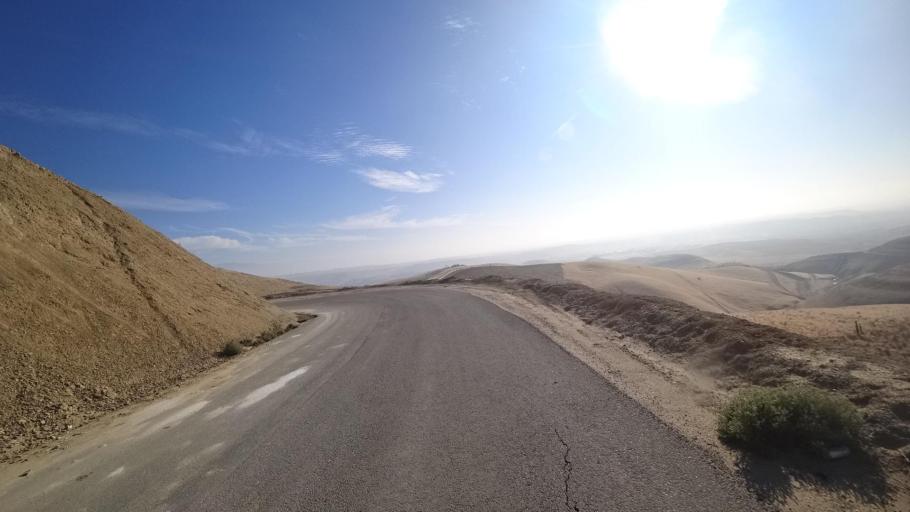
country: US
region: California
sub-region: Kern County
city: Oildale
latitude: 35.4717
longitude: -118.8717
